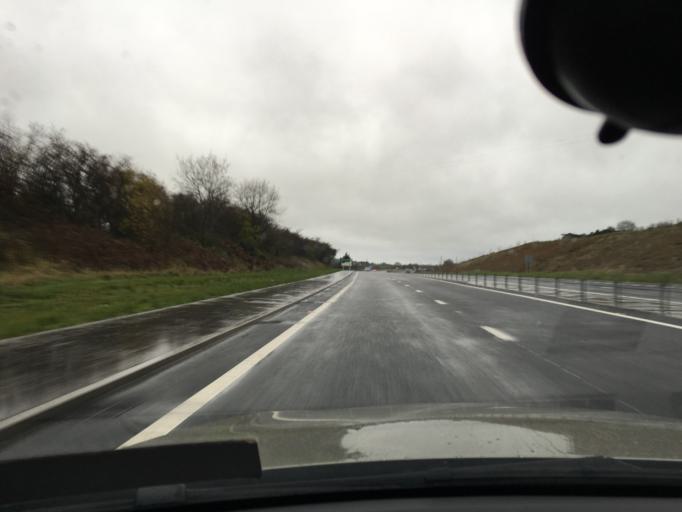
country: GB
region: Northern Ireland
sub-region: Larne District
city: Larne
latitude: 54.8109
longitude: -5.9060
